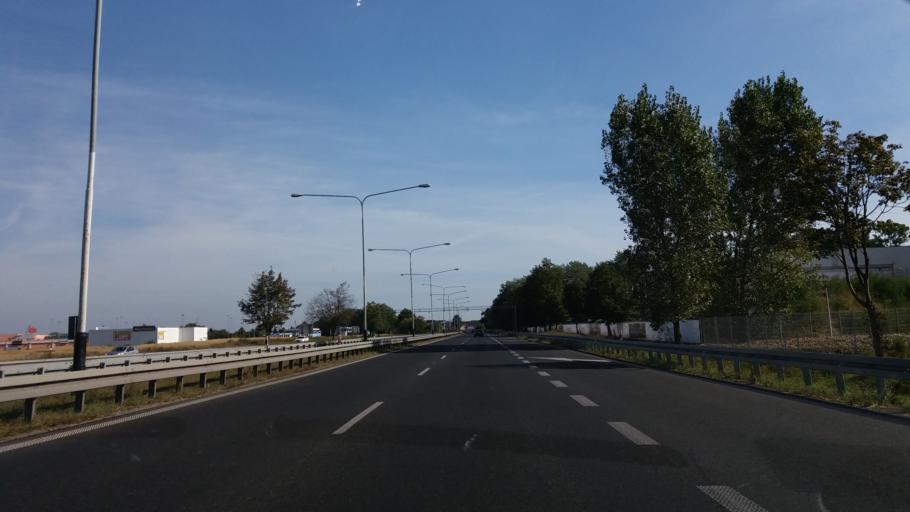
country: PL
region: Greater Poland Voivodeship
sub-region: Powiat poznanski
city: Baranowo
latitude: 52.4397
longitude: 16.7574
